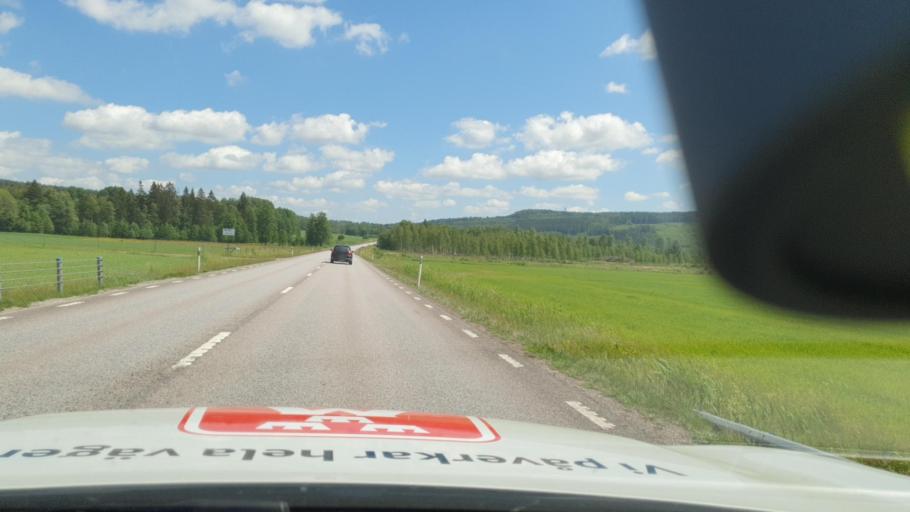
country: SE
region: Vaermland
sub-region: Karlstads Kommun
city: Molkom
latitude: 59.6062
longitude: 13.7556
